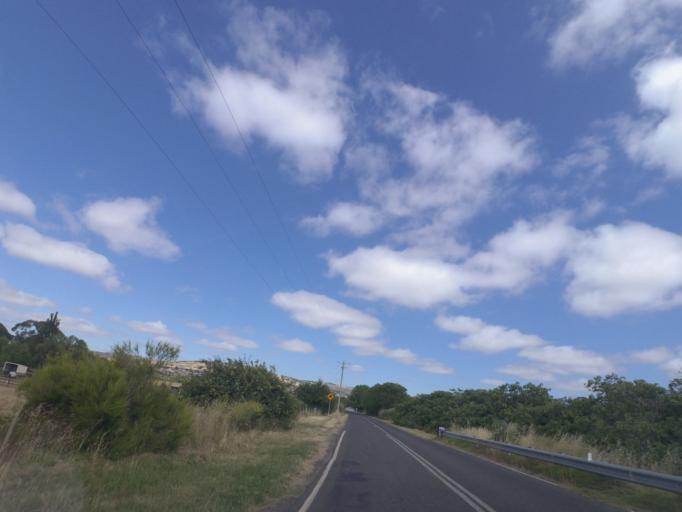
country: AU
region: Victoria
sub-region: Moorabool
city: Bacchus Marsh
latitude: -37.6462
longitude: 144.4478
